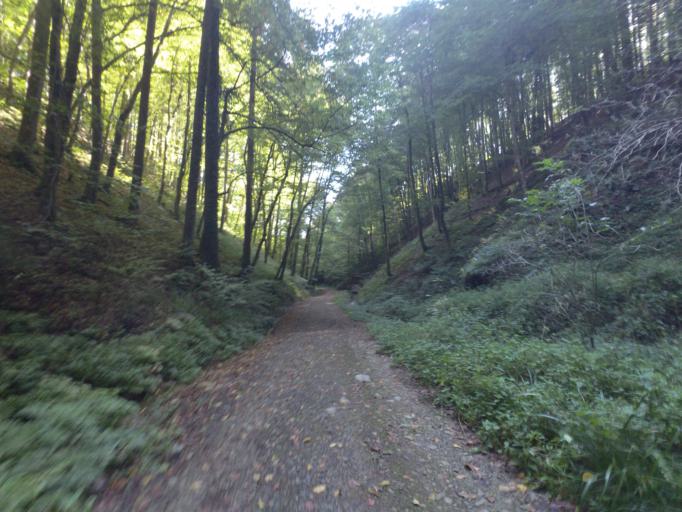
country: AT
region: Styria
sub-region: Politischer Bezirk Leibnitz
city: Kitzeck im Sausal
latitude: 46.7855
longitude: 15.4389
